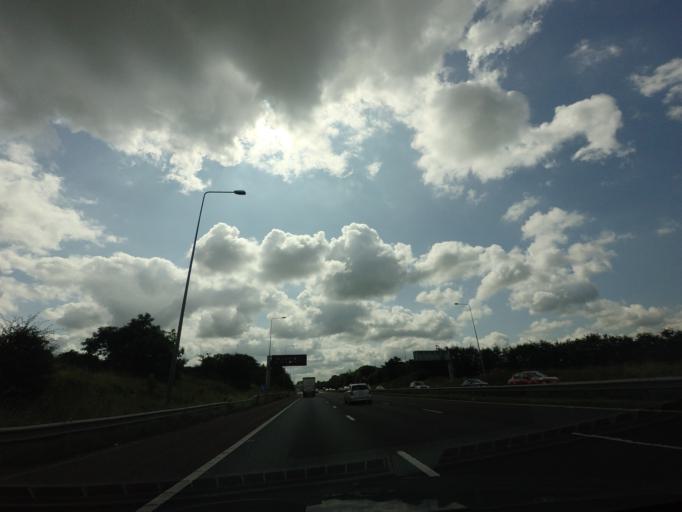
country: GB
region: England
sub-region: Lancashire
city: Euxton
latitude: 53.6381
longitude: -2.6921
